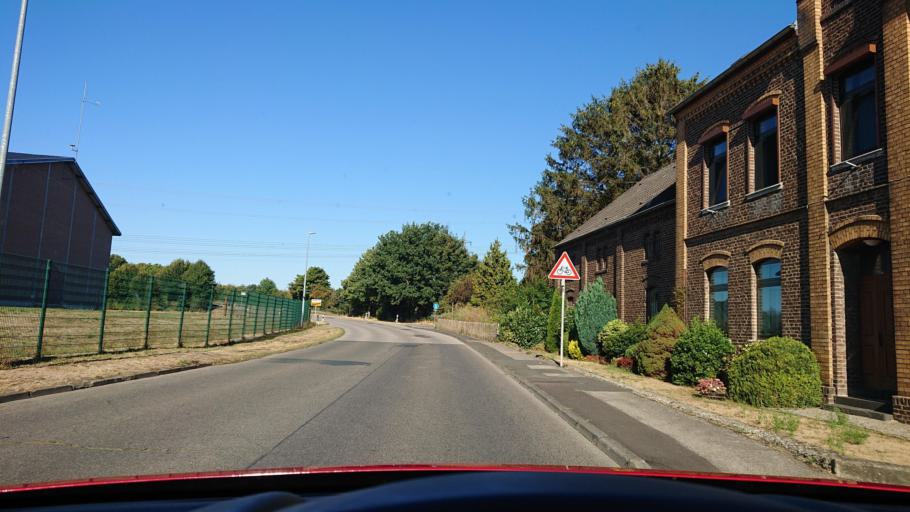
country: DE
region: North Rhine-Westphalia
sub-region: Regierungsbezirk Koln
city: Bergheim
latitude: 50.9243
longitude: 6.6196
